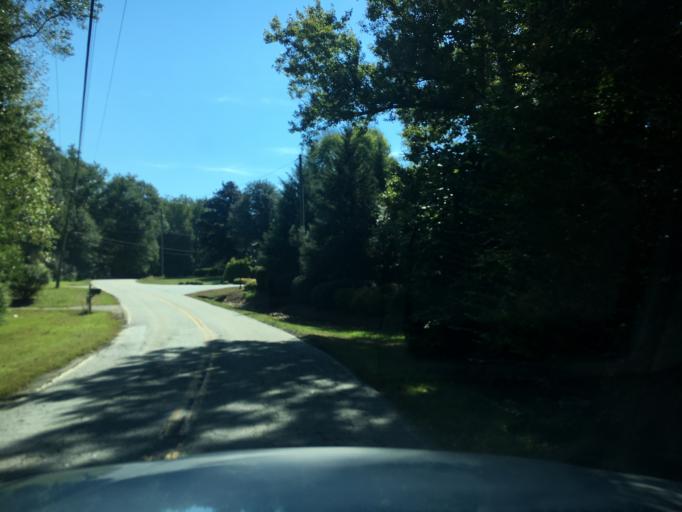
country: US
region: South Carolina
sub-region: Greenville County
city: Taylors
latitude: 34.9033
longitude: -82.2782
